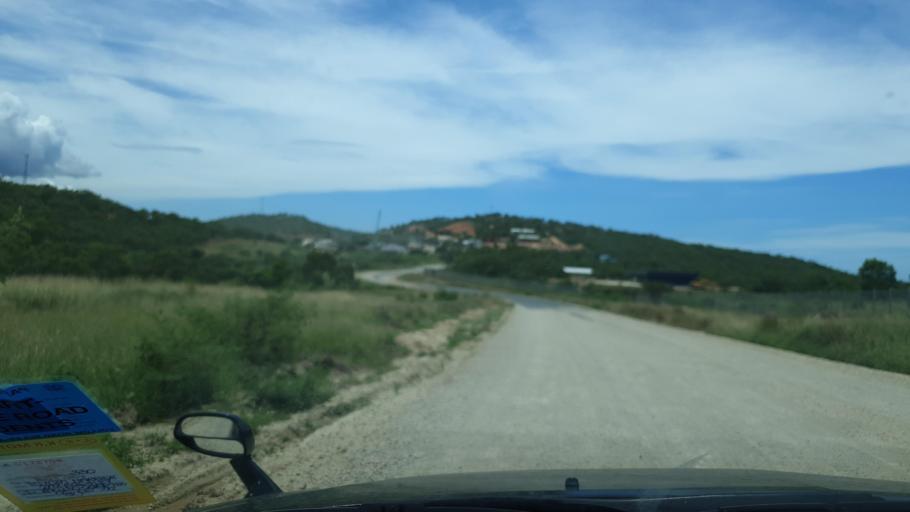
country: PG
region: National Capital
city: Port Moresby
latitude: -9.4441
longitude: 147.0779
